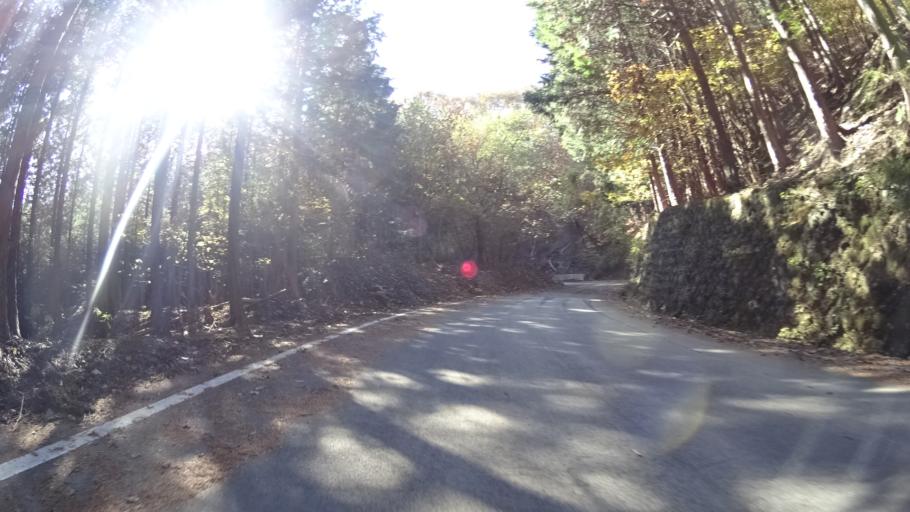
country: JP
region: Yamanashi
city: Otsuki
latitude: 35.7373
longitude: 138.9517
